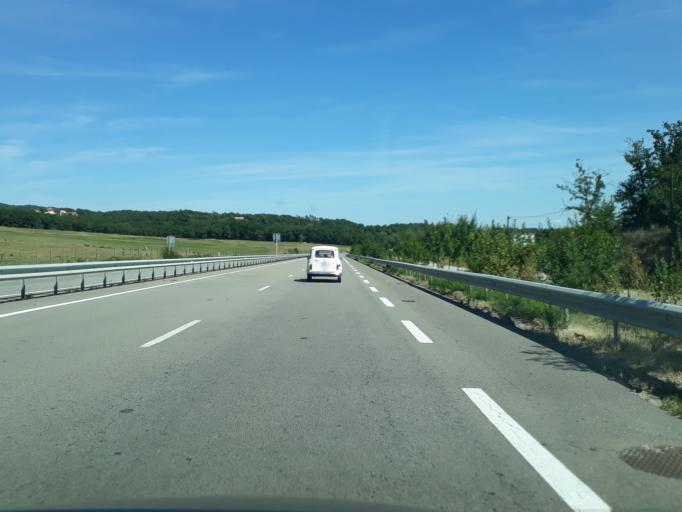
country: FR
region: Rhone-Alpes
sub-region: Departement de l'Ardeche
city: Davezieux
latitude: 45.2665
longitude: 4.7111
